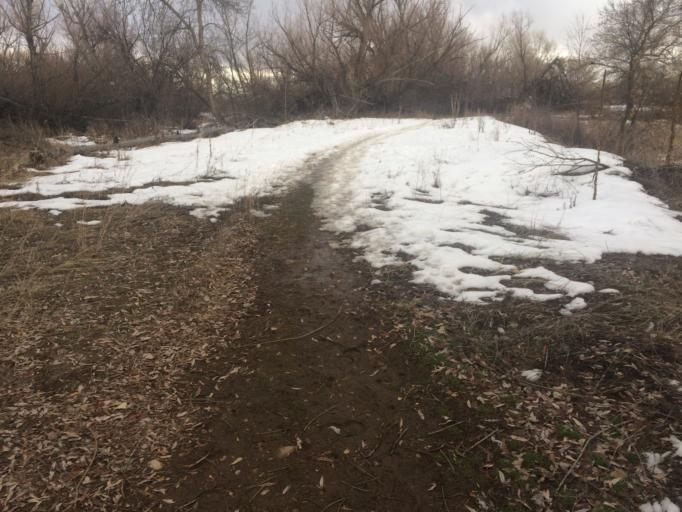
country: US
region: Colorado
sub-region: Boulder County
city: Gunbarrel
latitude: 40.0405
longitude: -105.1984
